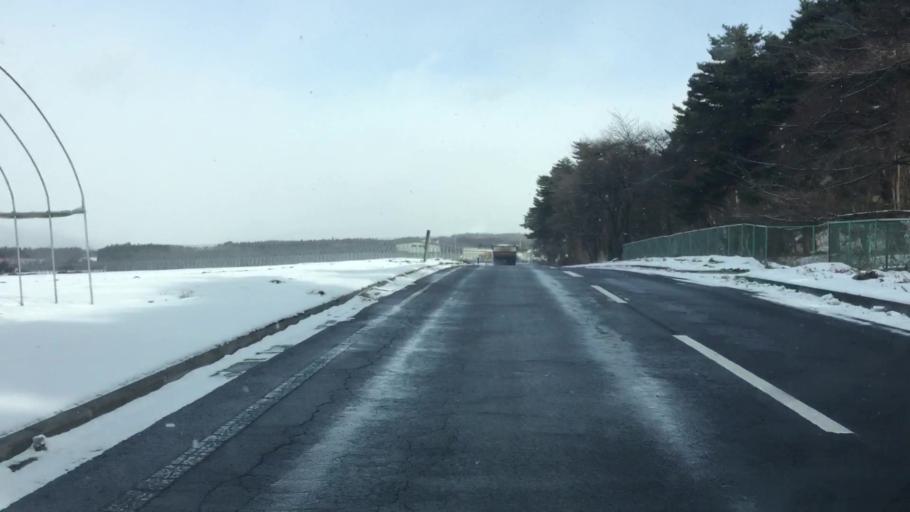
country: JP
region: Gunma
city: Numata
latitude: 36.6238
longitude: 139.0896
